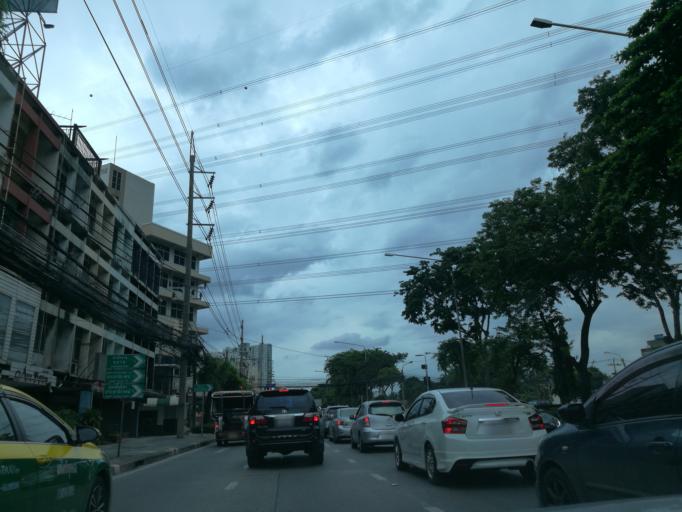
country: TH
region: Bangkok
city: Chatuchak
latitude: 13.8392
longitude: 100.5412
